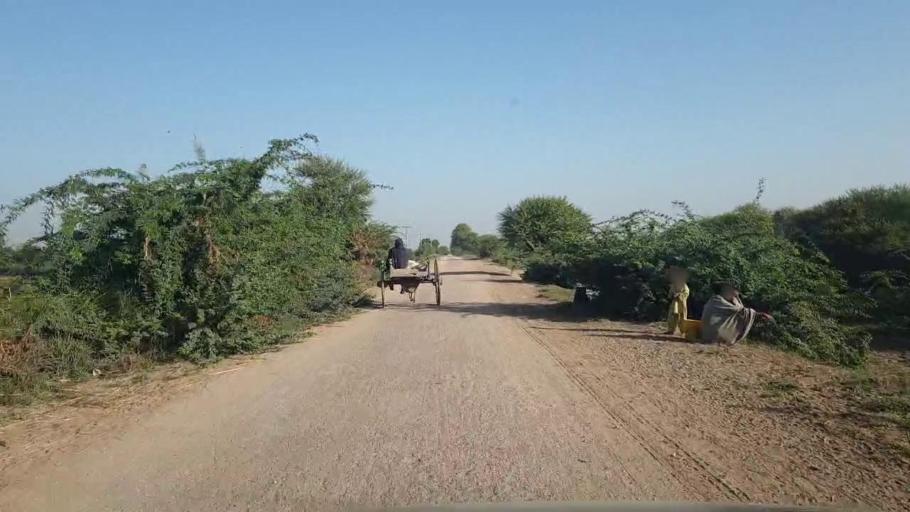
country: PK
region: Sindh
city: Badin
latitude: 24.6904
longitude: 68.8159
